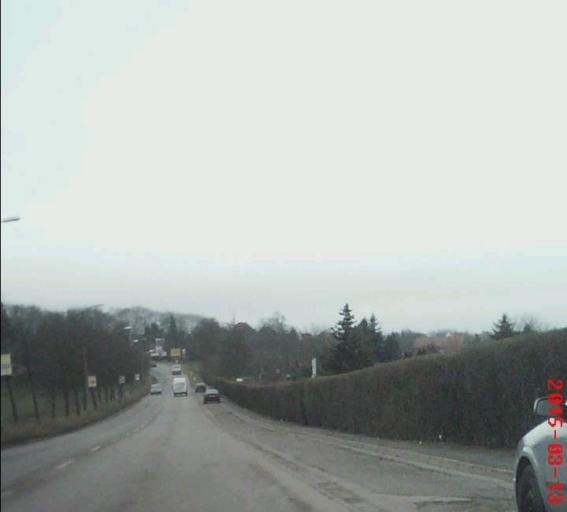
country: DE
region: Thuringia
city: Bad Langensalza
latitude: 51.1170
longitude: 10.6588
